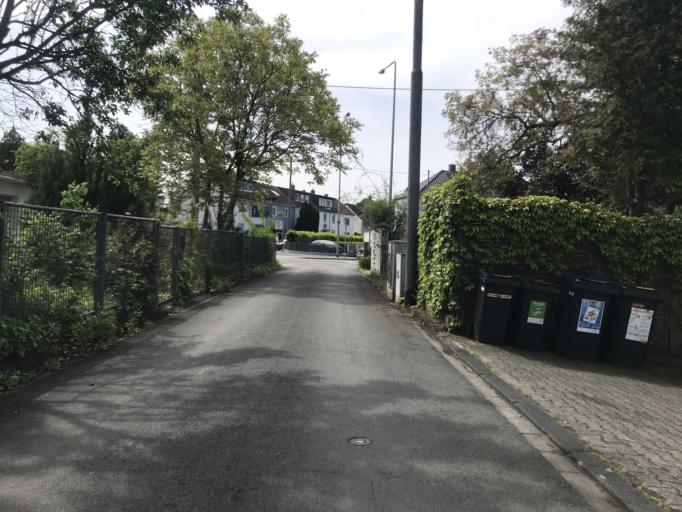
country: DE
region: Hesse
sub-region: Regierungsbezirk Darmstadt
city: Wiesbaden
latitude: 50.0468
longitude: 8.2259
